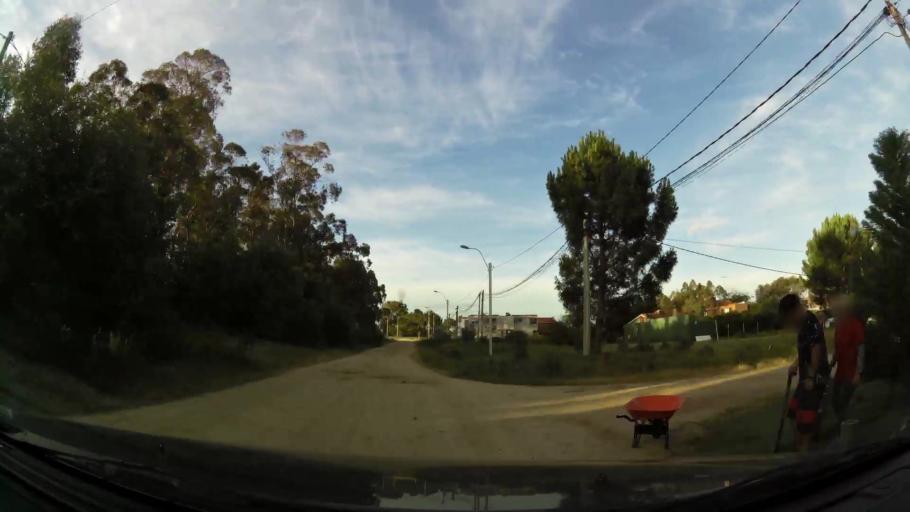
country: UY
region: Canelones
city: Atlantida
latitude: -34.7688
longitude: -55.7970
